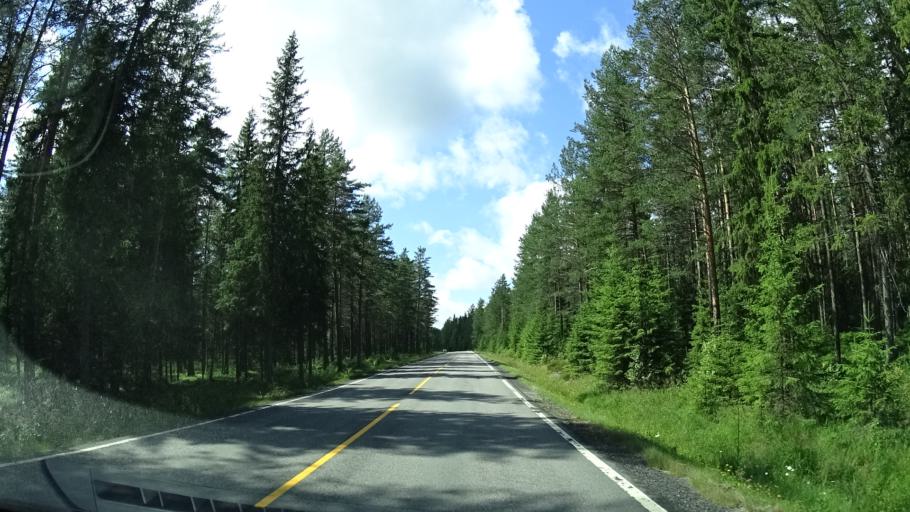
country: NO
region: Buskerud
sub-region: Krodsherad
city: Noresund
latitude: 60.1879
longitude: 9.7750
